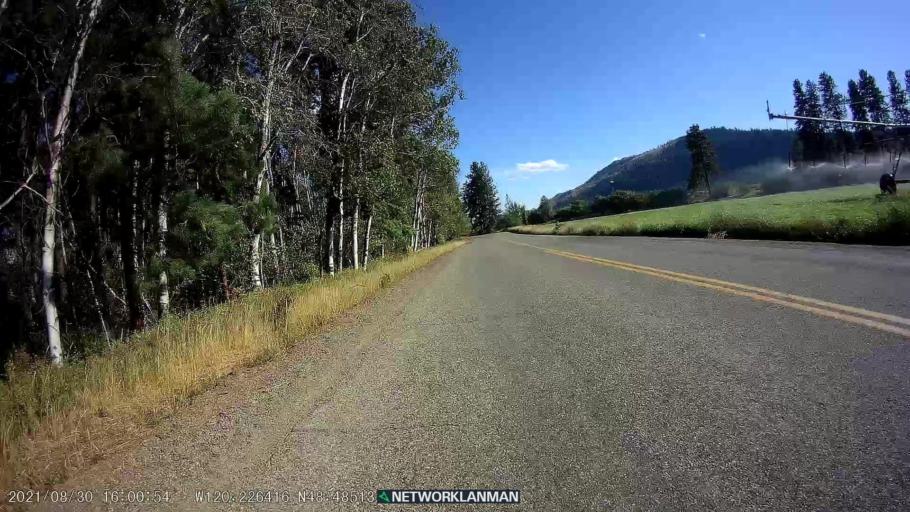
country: US
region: Washington
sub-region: Okanogan County
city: Brewster
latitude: 48.4855
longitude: -120.2267
